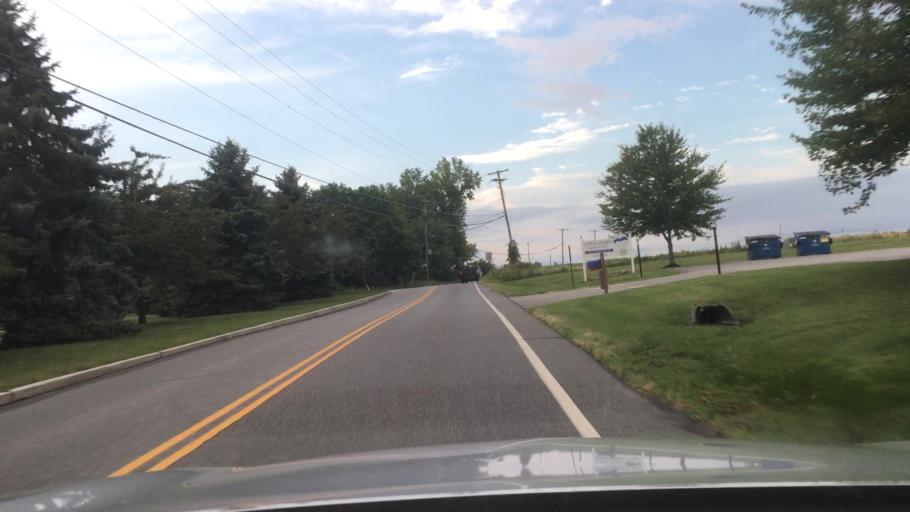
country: US
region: Pennsylvania
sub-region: York County
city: Dillsburg
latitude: 40.1255
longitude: -77.0172
